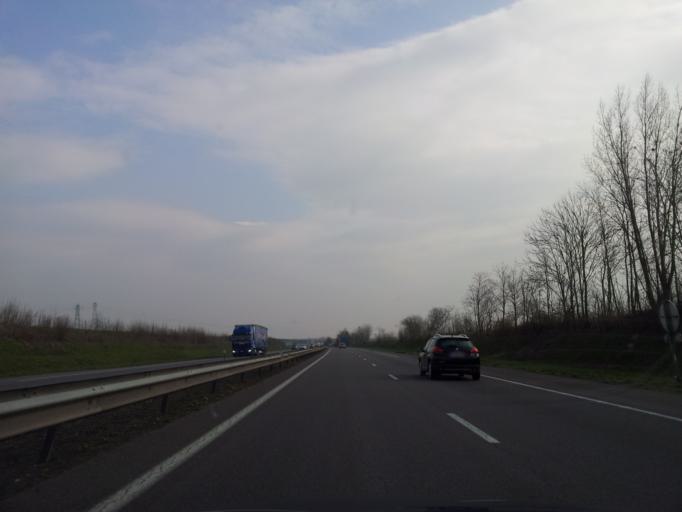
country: FR
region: Alsace
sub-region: Departement du Bas-Rhin
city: Mommenheim
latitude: 48.7584
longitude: 7.6692
